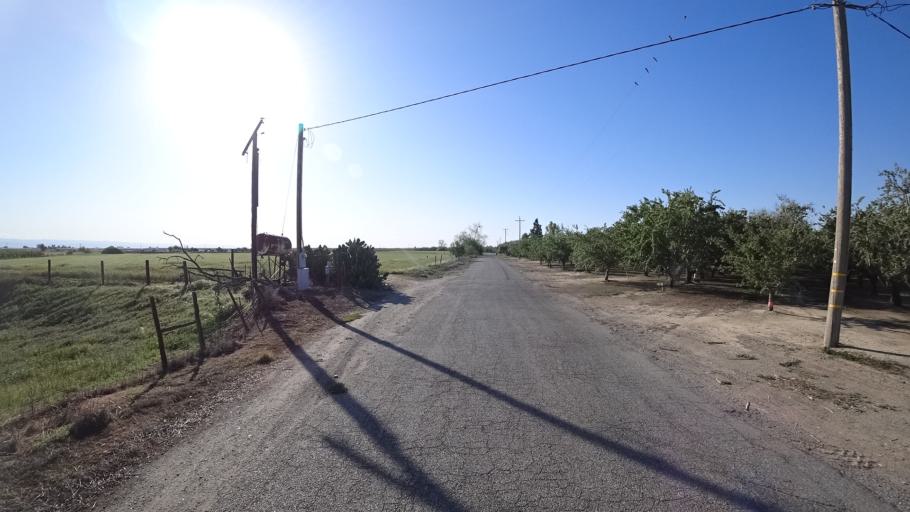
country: US
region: California
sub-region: Glenn County
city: Orland
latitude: 39.7176
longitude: -122.1676
